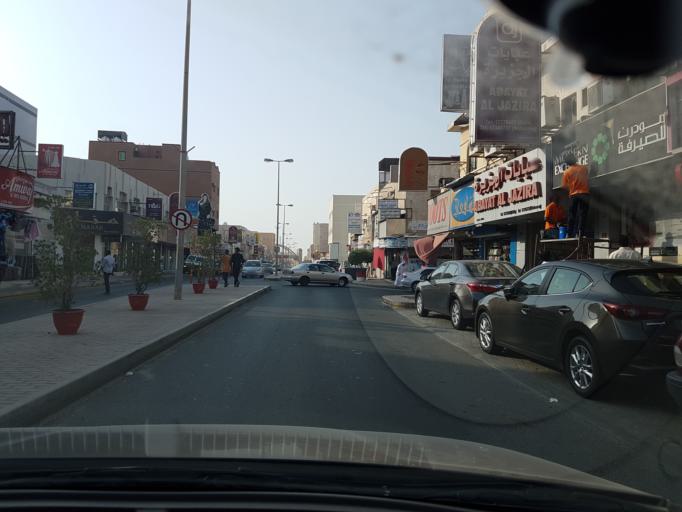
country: BH
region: Northern
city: Ar Rifa'
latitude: 26.1225
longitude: 50.5661
